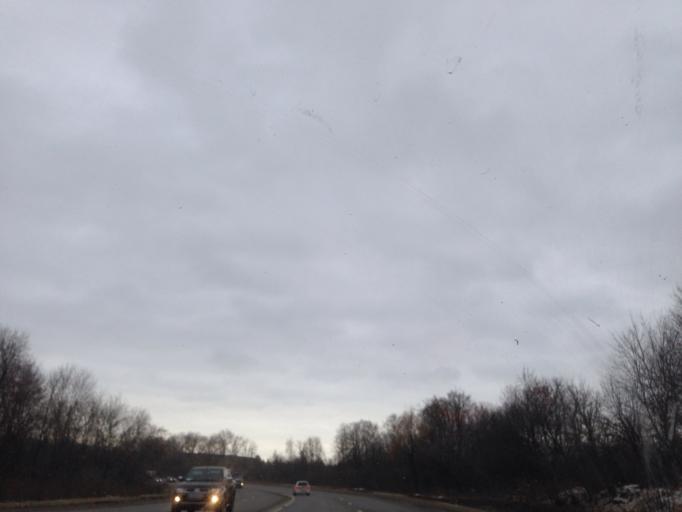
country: RU
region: Tula
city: Tula
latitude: 54.1495
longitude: 37.6415
